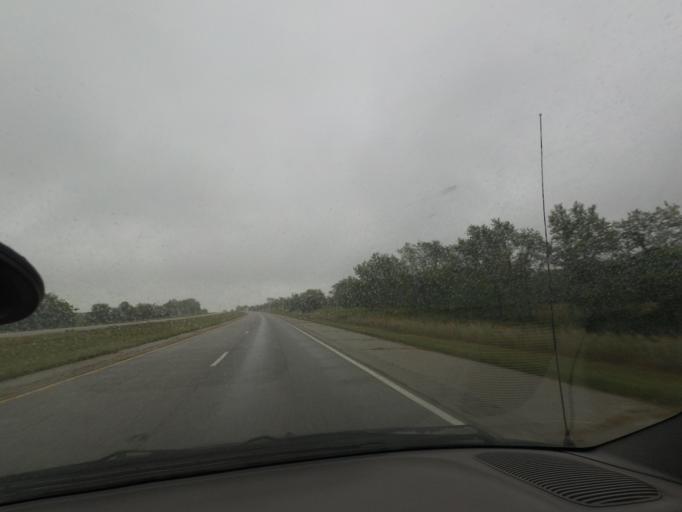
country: US
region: Illinois
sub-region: Pike County
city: Barry
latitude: 39.6928
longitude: -90.9972
